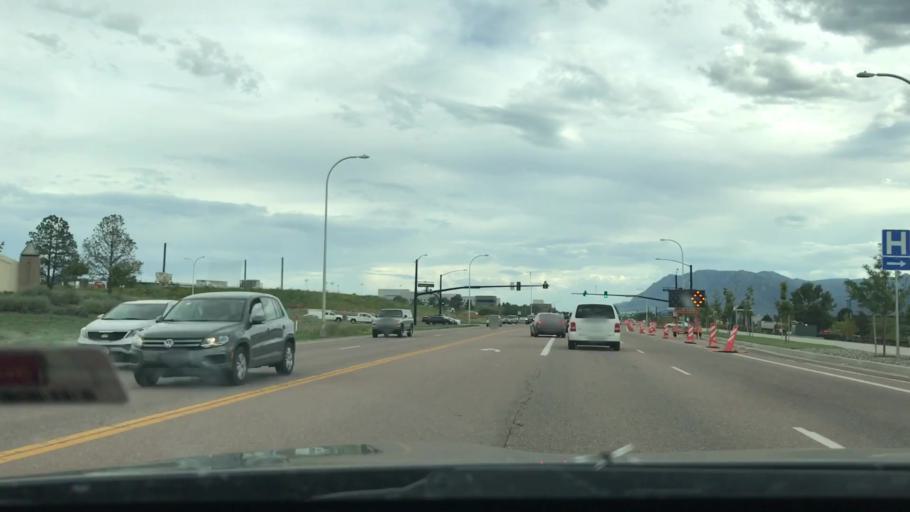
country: US
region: Colorado
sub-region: El Paso County
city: Colorado Springs
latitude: 38.9115
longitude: -104.8161
